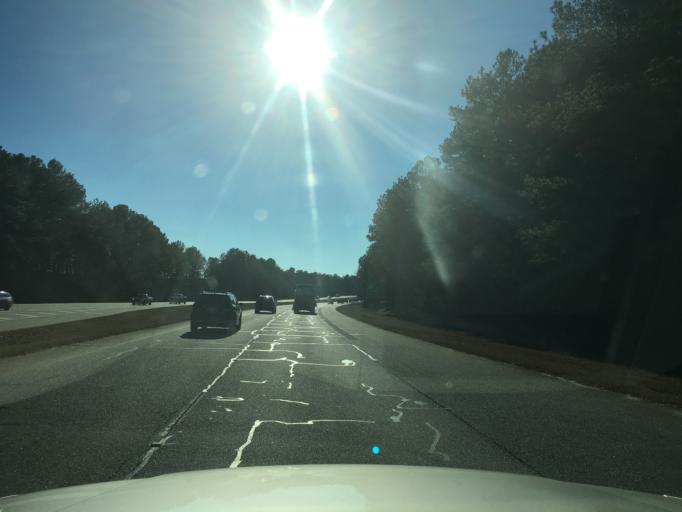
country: US
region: Georgia
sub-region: Carroll County
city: Carrollton
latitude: 33.5617
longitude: -85.0573
